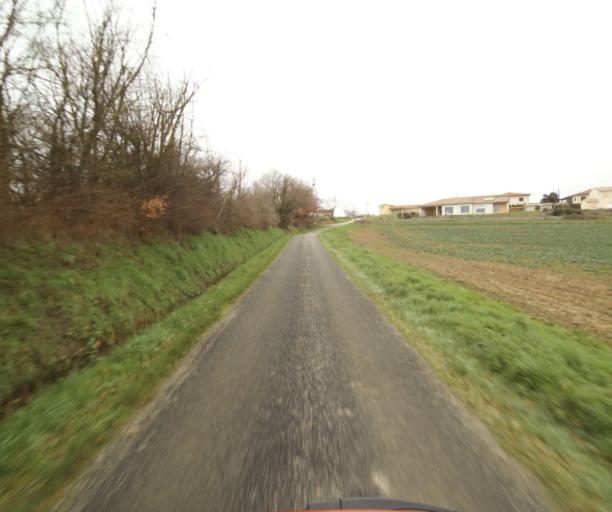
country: FR
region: Midi-Pyrenees
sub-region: Departement de la Haute-Garonne
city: Gaillac-Toulza
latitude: 43.2589
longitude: 1.5183
